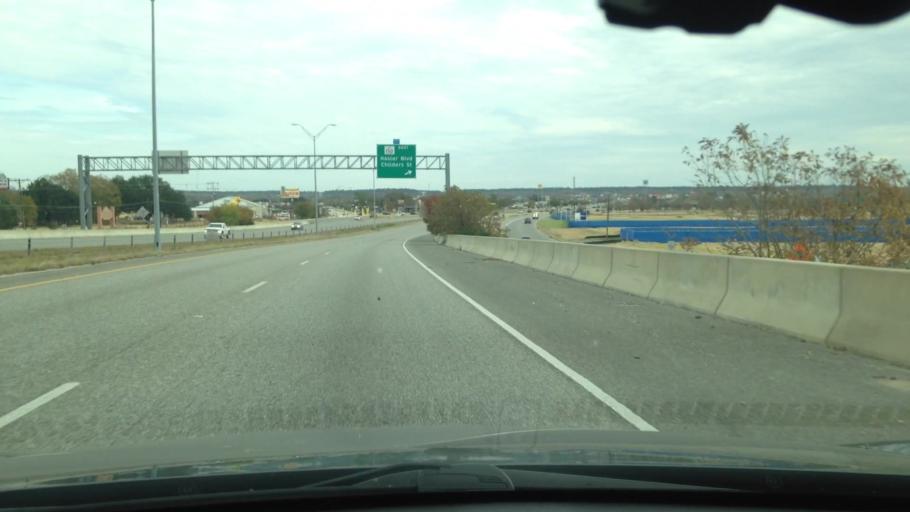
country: US
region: Texas
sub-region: Bastrop County
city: Bastrop
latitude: 30.1111
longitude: -97.3486
